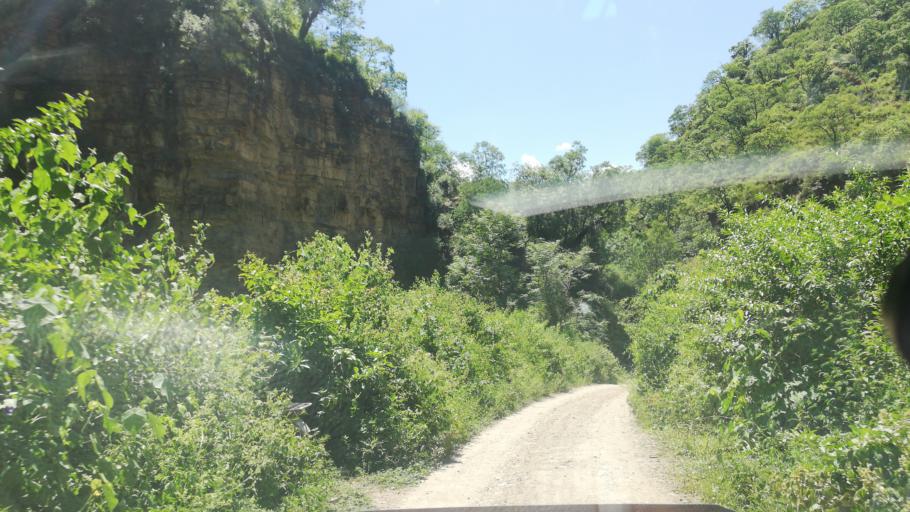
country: BO
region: Cochabamba
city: Mizque
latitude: -17.8306
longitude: -65.3058
